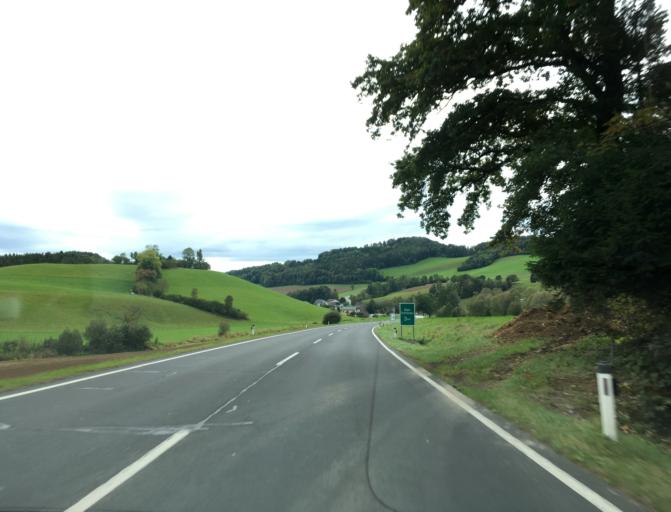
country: AT
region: Lower Austria
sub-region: Politischer Bezirk Wiener Neustadt
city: Bad Schonau
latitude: 47.5096
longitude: 16.2022
